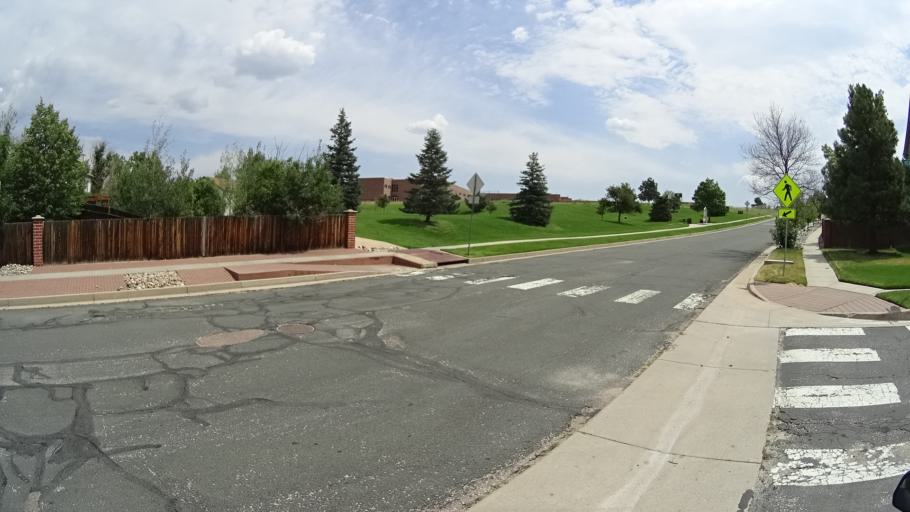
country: US
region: Colorado
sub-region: El Paso County
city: Air Force Academy
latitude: 38.9637
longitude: -104.7787
